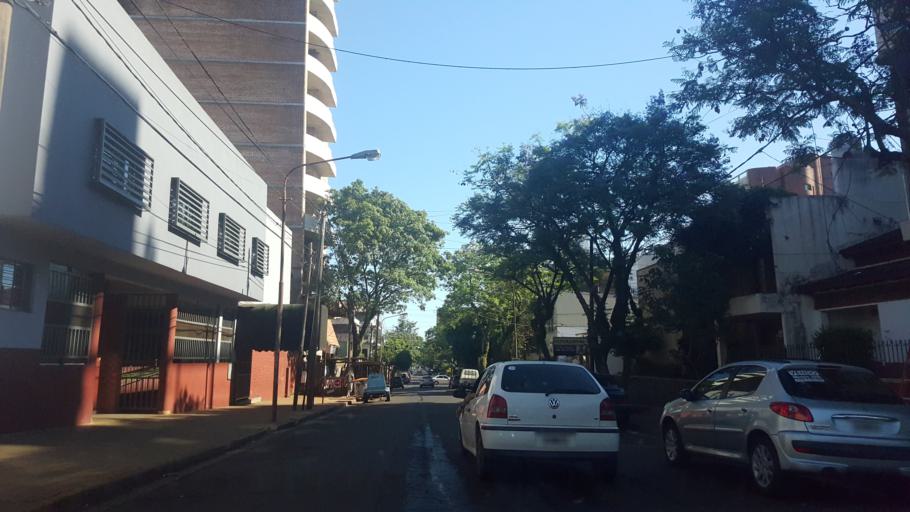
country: AR
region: Misiones
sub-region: Departamento de Capital
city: Posadas
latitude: -27.3721
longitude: -55.8996
